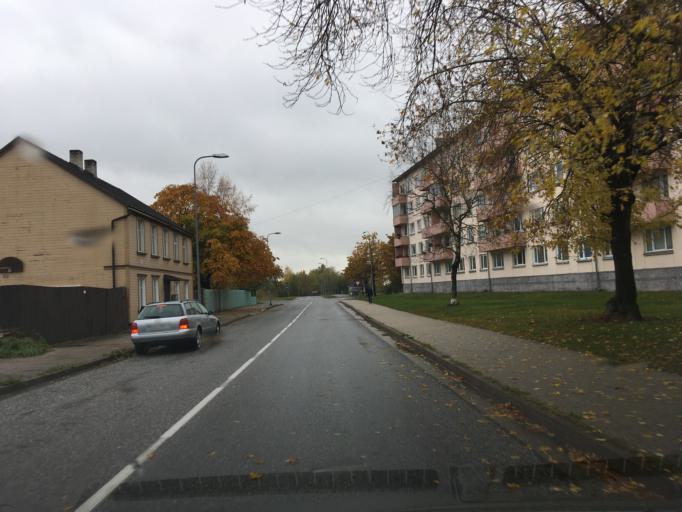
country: EE
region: Paernumaa
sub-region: Paernu linn
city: Parnu
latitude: 58.3746
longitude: 24.5168
